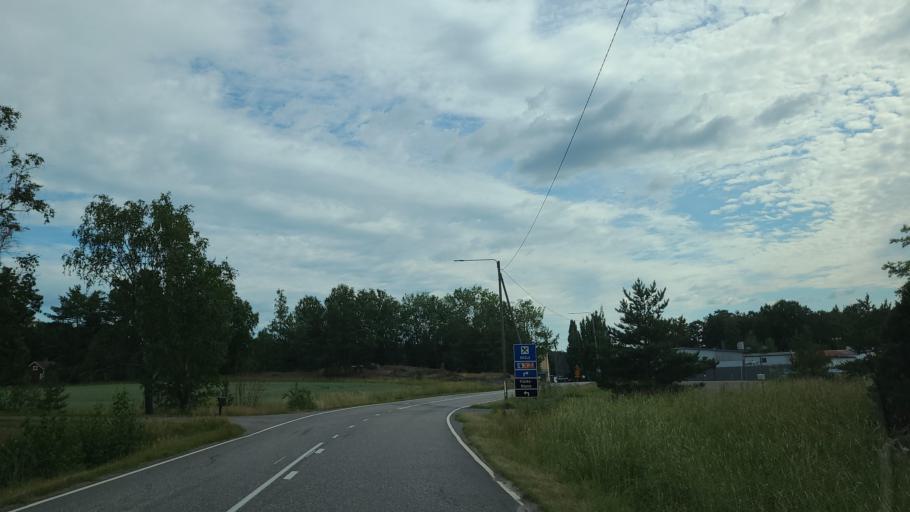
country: FI
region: Varsinais-Suomi
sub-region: Turku
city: Rymaettylae
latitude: 60.3488
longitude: 21.9571
